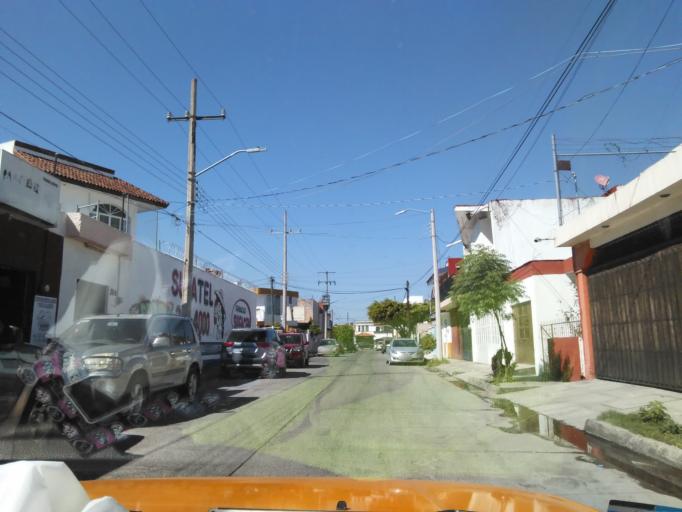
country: MX
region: Nayarit
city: Tepic
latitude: 21.4971
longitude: -104.8877
